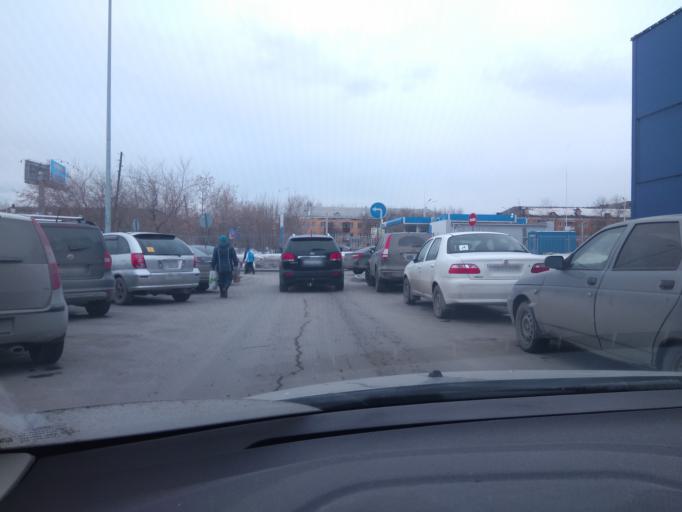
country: RU
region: Sverdlovsk
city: Yekaterinburg
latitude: 56.9126
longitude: 60.6142
